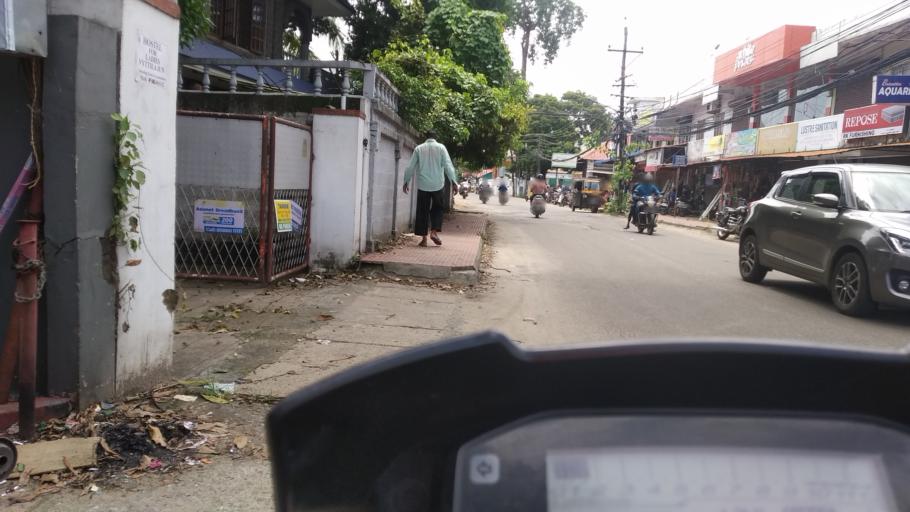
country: IN
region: Kerala
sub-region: Ernakulam
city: Cochin
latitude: 9.9922
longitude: 76.3089
